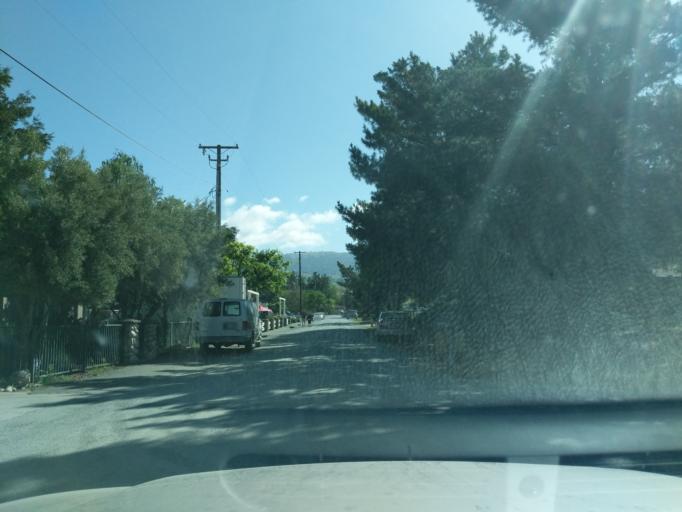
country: US
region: California
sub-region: Santa Clara County
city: San Martin
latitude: 37.0874
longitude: -121.5798
